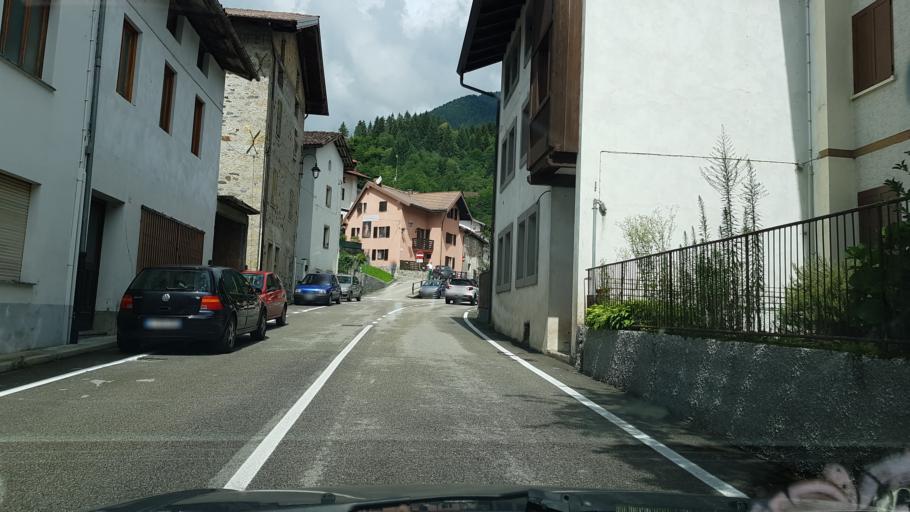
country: IT
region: Friuli Venezia Giulia
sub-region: Provincia di Udine
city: Cercivento
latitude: 46.5268
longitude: 12.9951
